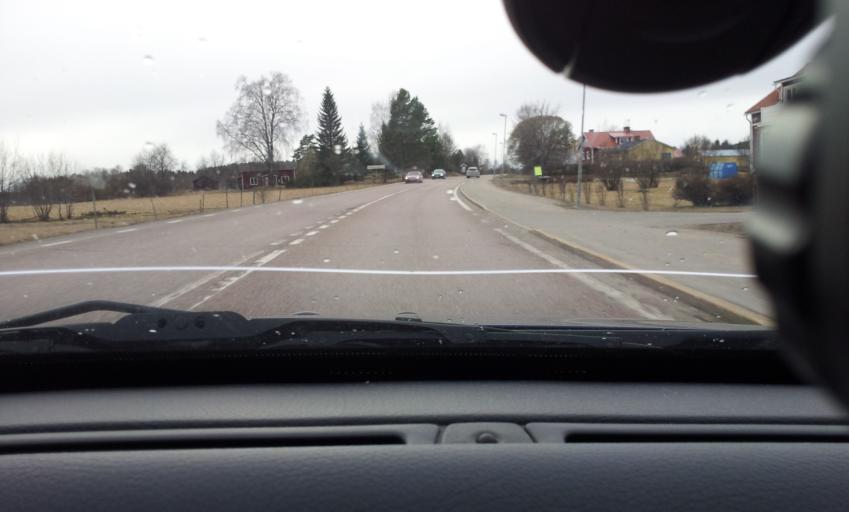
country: SE
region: Gaevleborg
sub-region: Ljusdals Kommun
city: Farila
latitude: 61.8004
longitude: 15.8895
